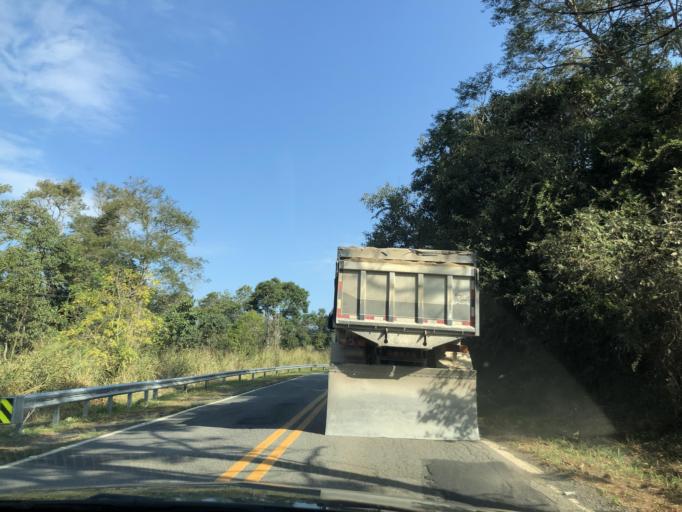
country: BR
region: Sao Paulo
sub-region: Pilar Do Sul
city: Pilar do Sul
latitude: -23.8083
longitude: -47.6946
